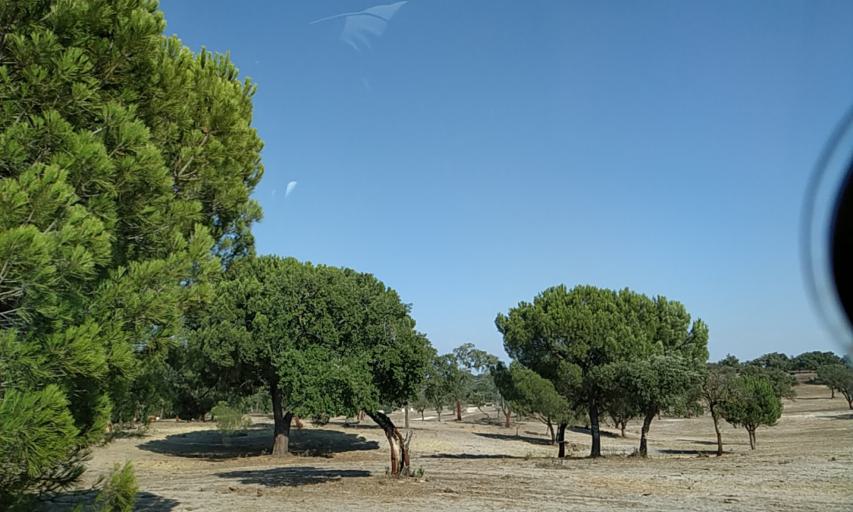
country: PT
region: Santarem
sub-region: Coruche
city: Coruche
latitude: 38.8495
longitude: -8.5454
